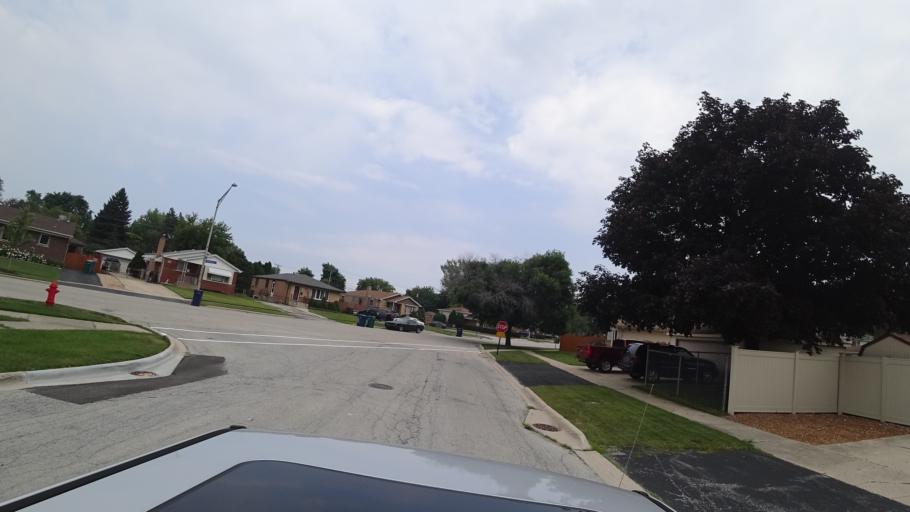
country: US
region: Illinois
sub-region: Cook County
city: Chicago Ridge
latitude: 41.7000
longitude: -87.7738
